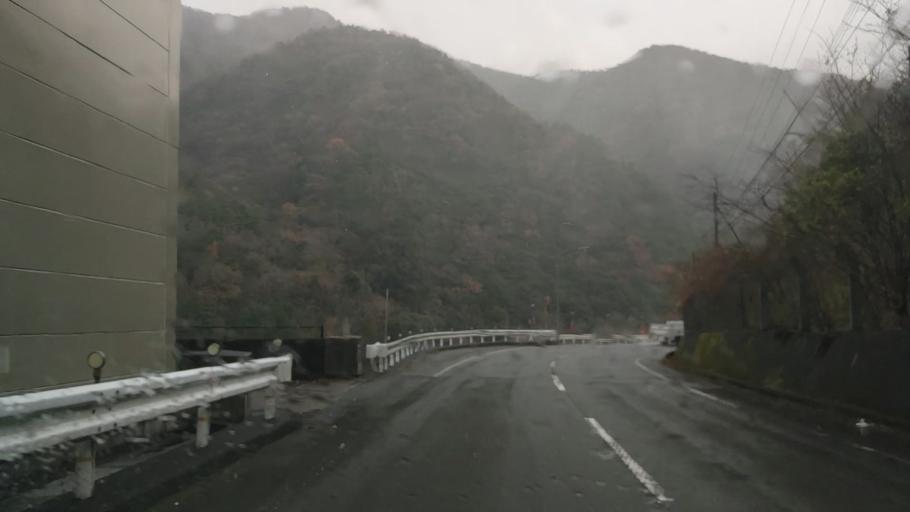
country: JP
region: Tokushima
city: Kamojimacho-jogejima
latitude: 34.1474
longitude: 134.3542
